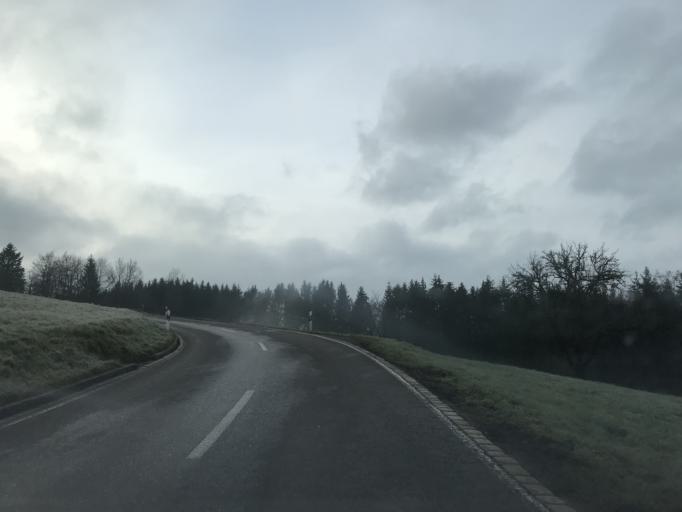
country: DE
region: Baden-Wuerttemberg
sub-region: Freiburg Region
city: Wehr
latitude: 47.6217
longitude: 7.9102
